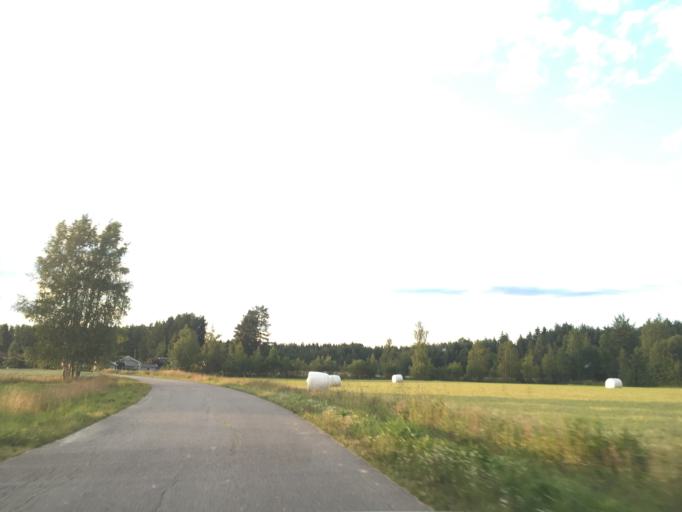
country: NO
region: Akershus
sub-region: Nes
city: Fjellfoten
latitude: 60.0960
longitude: 11.4898
